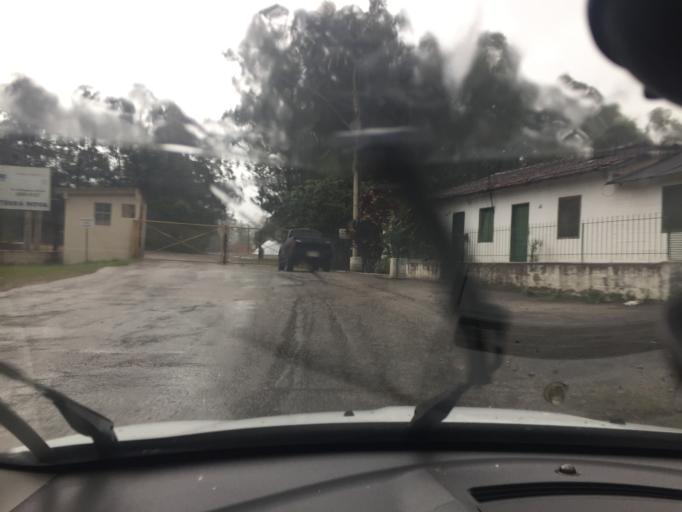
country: BR
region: Sao Paulo
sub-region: Varzea Paulista
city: Varzea Paulista
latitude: -23.2662
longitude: -46.8761
